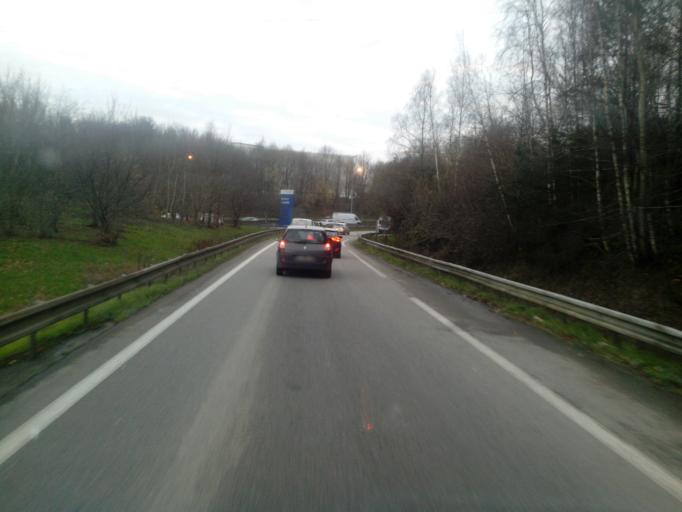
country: FR
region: Pays de la Loire
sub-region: Departement de la Loire-Atlantique
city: La Chapelle-sur-Erdre
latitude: 47.2689
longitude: -1.5635
